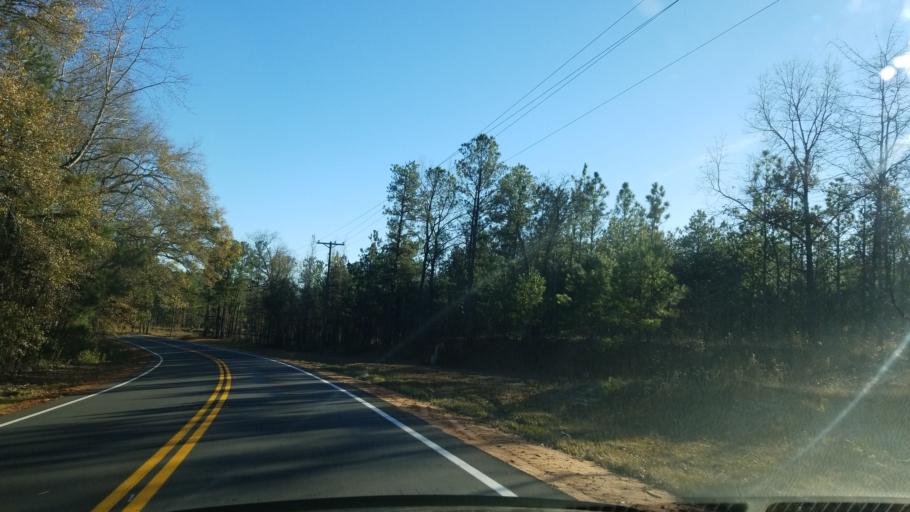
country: US
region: Georgia
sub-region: Talbot County
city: Talbotton
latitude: 32.5612
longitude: -84.5427
